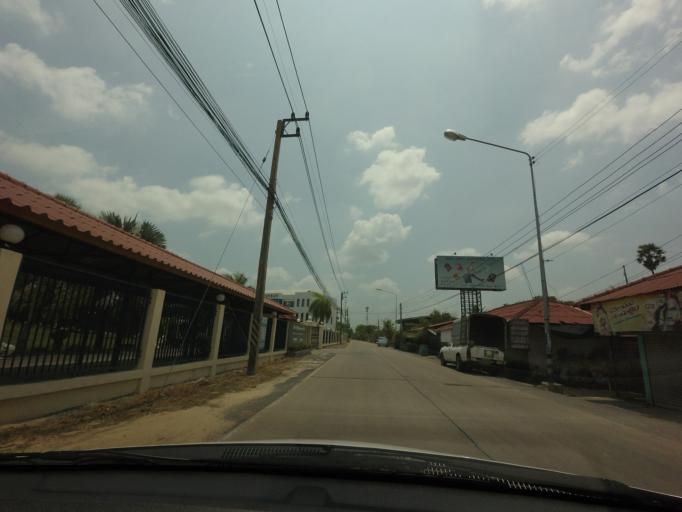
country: TH
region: Pathum Thani
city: Sam Khok
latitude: 14.0437
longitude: 100.5383
